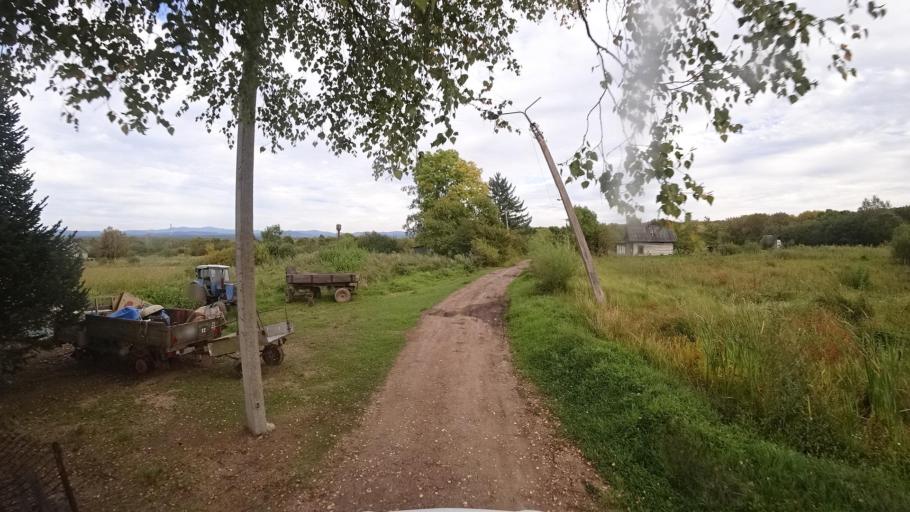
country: RU
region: Primorskiy
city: Dostoyevka
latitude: 44.3456
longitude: 133.4074
